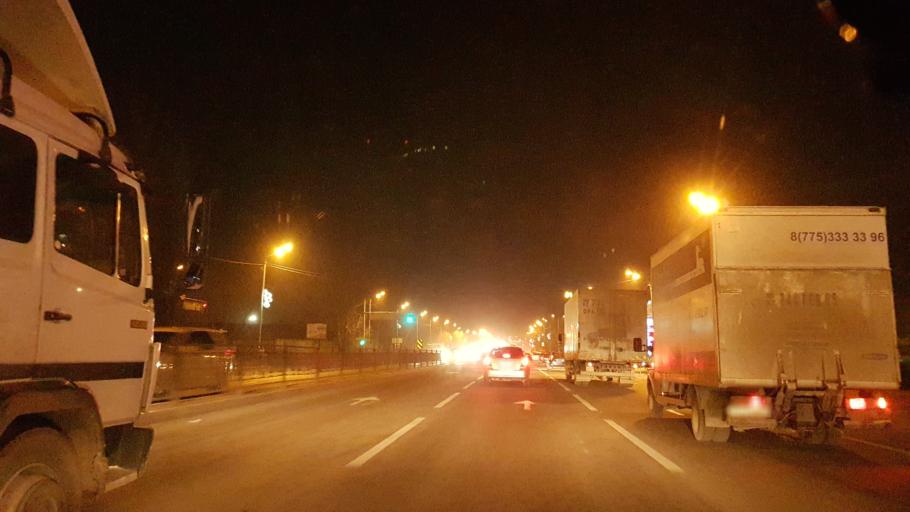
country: KZ
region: Almaty Qalasy
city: Almaty
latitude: 43.2661
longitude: 76.8685
